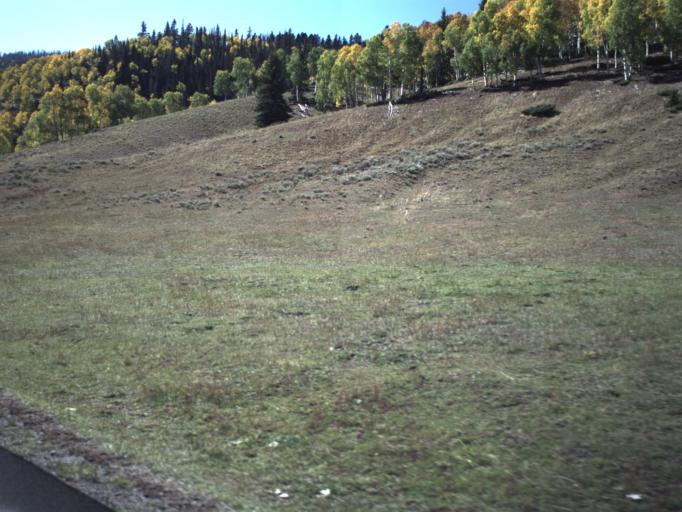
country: US
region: Utah
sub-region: Beaver County
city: Beaver
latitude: 38.2977
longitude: -112.4372
